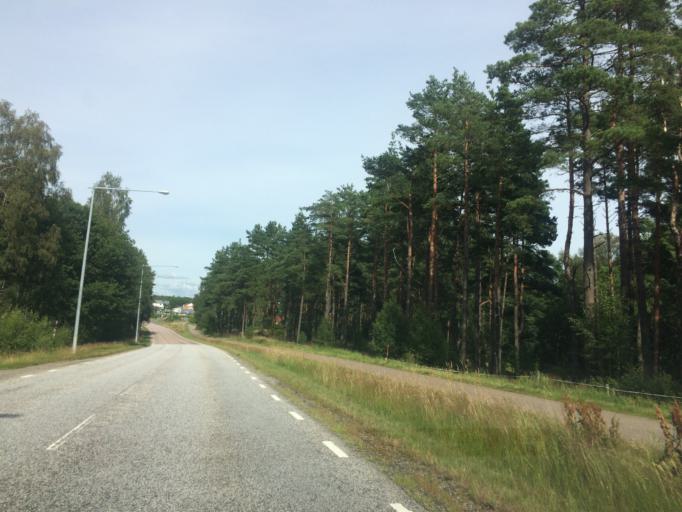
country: SE
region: Vaestra Goetaland
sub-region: Partille Kommun
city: Ojersjo
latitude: 57.6856
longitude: 12.1045
